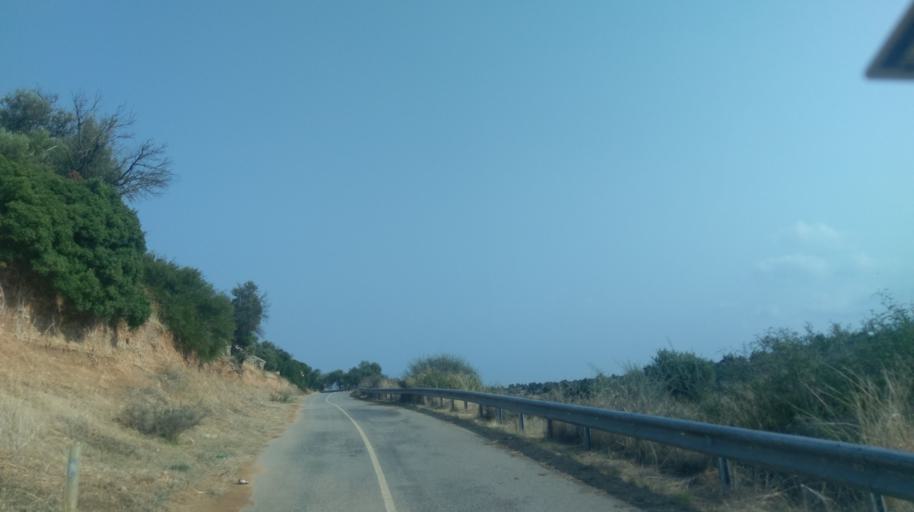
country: CY
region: Keryneia
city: Kyrenia
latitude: 35.3203
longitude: 33.4683
